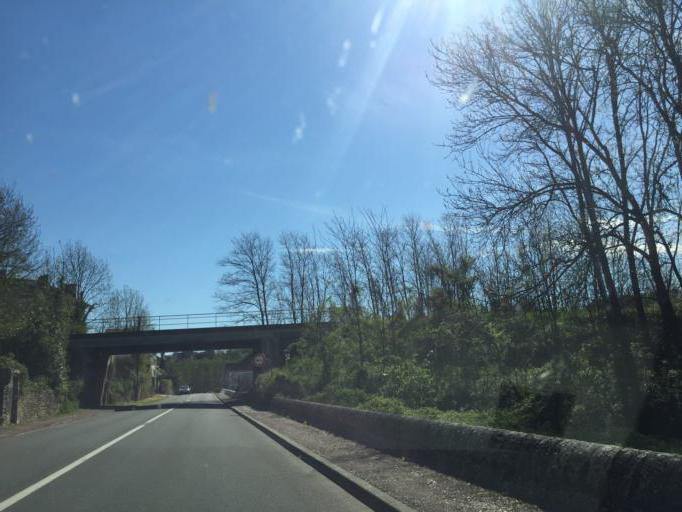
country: FR
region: Bourgogne
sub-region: Departement de la Nievre
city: Clamecy
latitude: 47.4570
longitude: 3.5116
